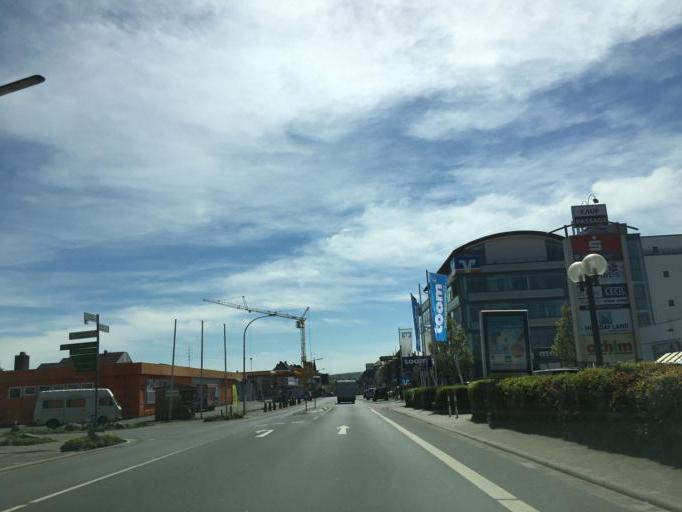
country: DE
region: Hesse
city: Reinheim
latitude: 49.8329
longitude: 8.8336
